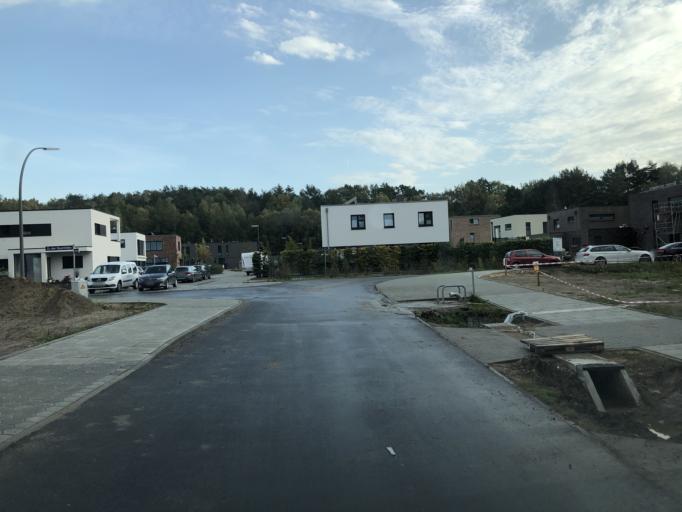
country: DE
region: Lower Saxony
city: Neu Wulmstorf
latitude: 53.4648
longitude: 9.8160
